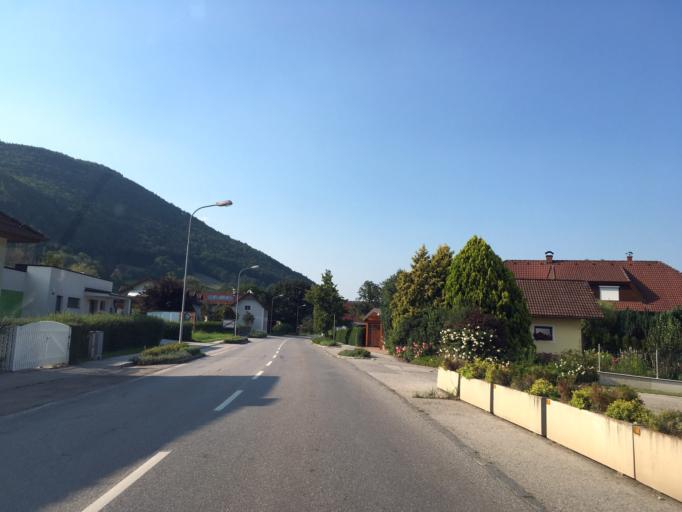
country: AT
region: Lower Austria
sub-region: Politischer Bezirk Neunkirchen
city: Grimmenstein
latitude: 47.6200
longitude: 16.1281
